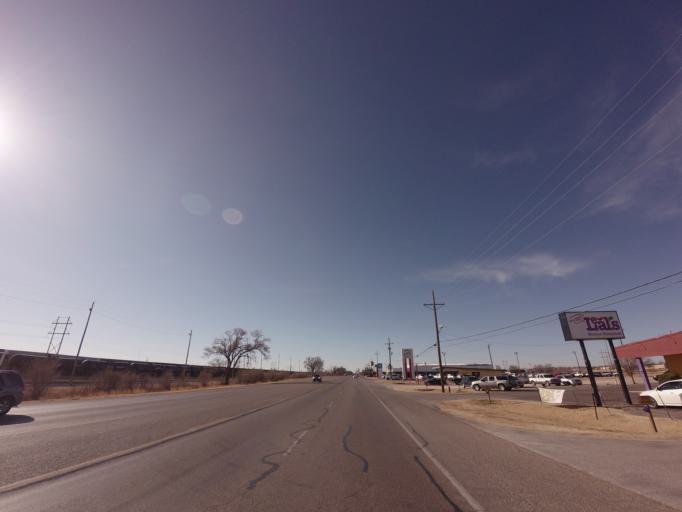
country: US
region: New Mexico
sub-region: Curry County
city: Clovis
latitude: 34.3954
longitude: -103.1636
